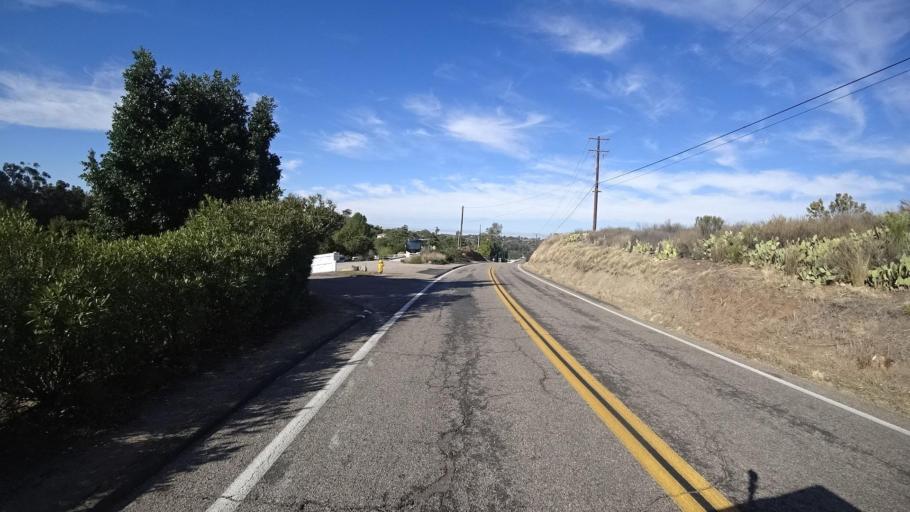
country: US
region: California
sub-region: San Diego County
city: Alpine
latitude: 32.8158
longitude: -116.7656
